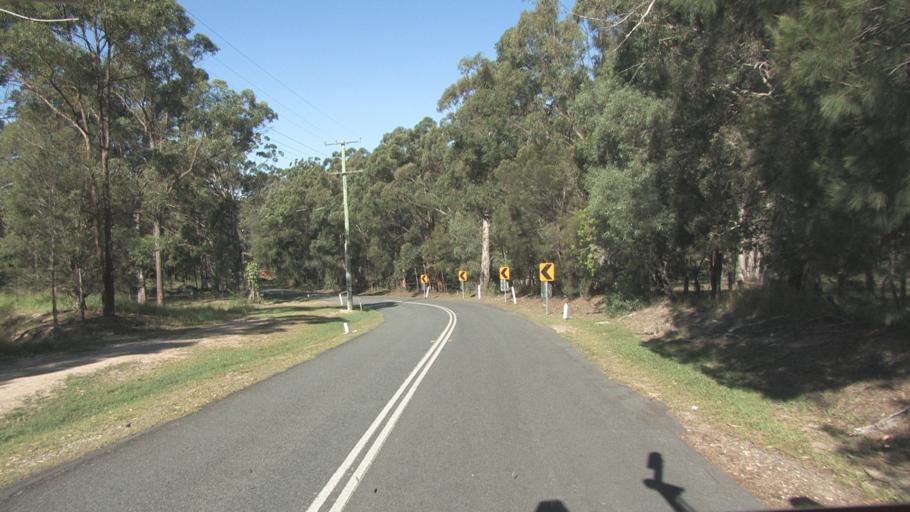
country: AU
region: Queensland
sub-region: Logan
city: Springwood
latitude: -27.5972
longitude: 153.1616
